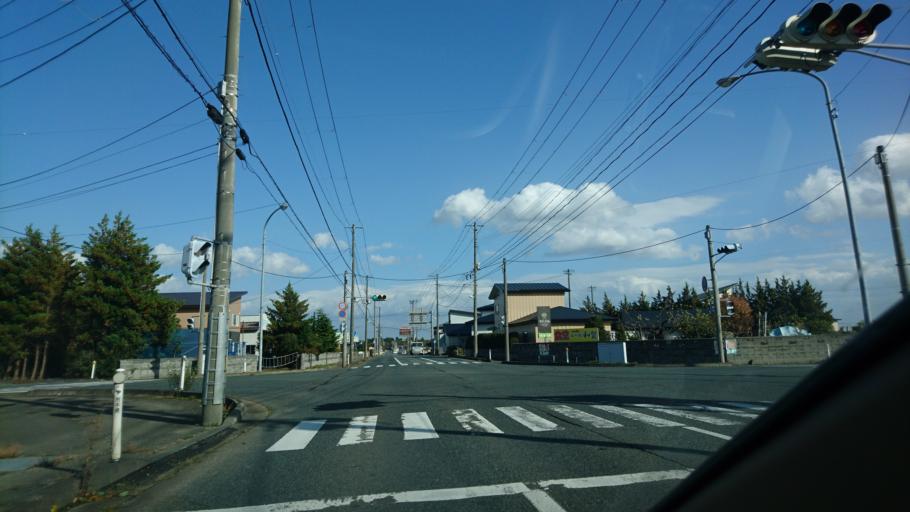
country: JP
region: Iwate
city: Kitakami
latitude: 39.3084
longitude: 140.9768
